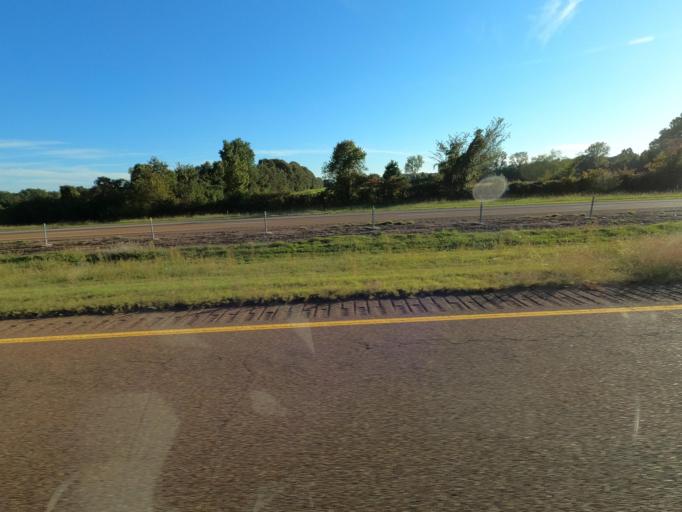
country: US
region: Tennessee
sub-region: Shelby County
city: Millington
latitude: 35.3085
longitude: -89.8098
